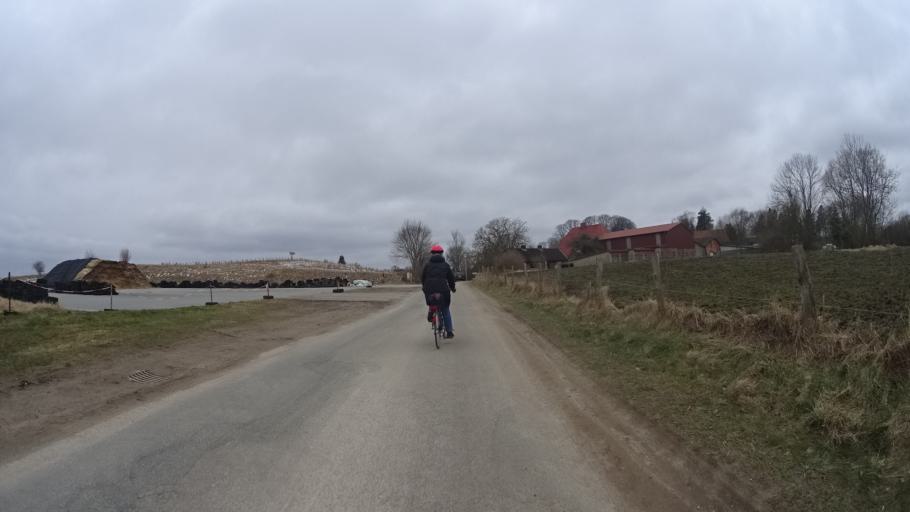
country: DE
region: Schleswig-Holstein
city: Neukirchen
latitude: 54.2211
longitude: 10.5603
